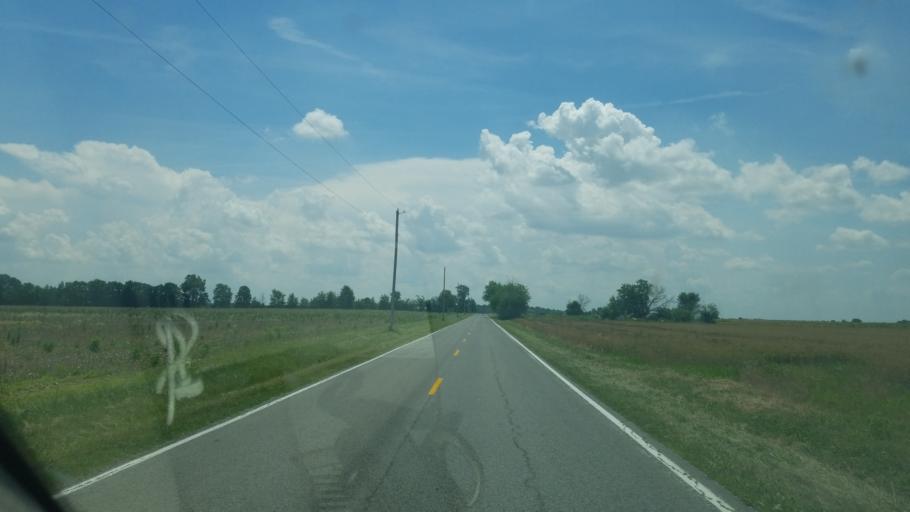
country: US
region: Ohio
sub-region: Hancock County
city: Arlington
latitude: 40.9029
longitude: -83.5947
